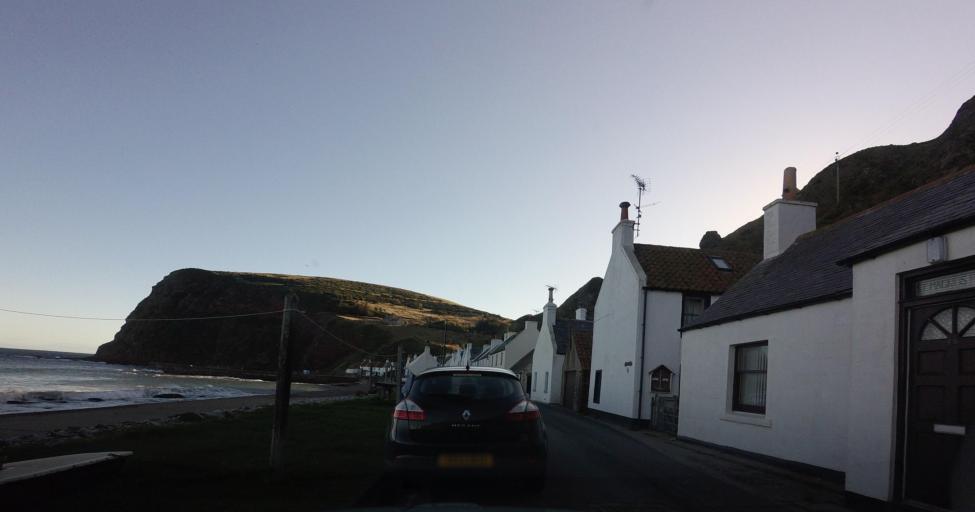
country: GB
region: Scotland
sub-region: Aberdeenshire
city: Rosehearty
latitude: 57.6790
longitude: -2.2619
